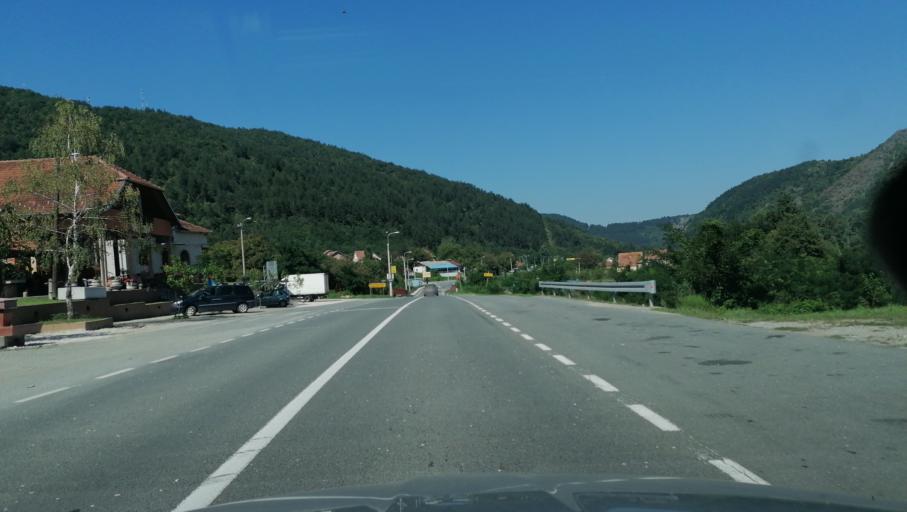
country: RS
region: Central Serbia
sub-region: Raski Okrug
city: Kraljevo
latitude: 43.6481
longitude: 20.5534
